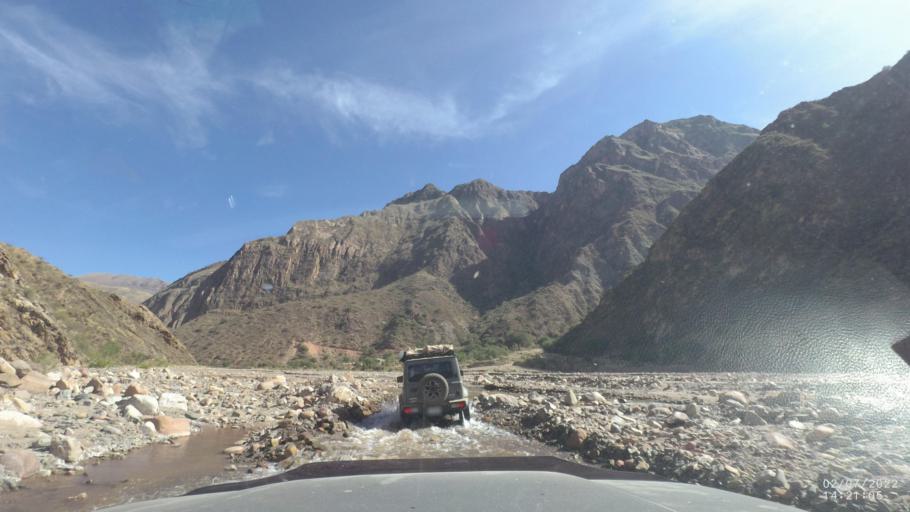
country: BO
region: Cochabamba
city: Irpa Irpa
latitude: -17.8287
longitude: -66.4119
